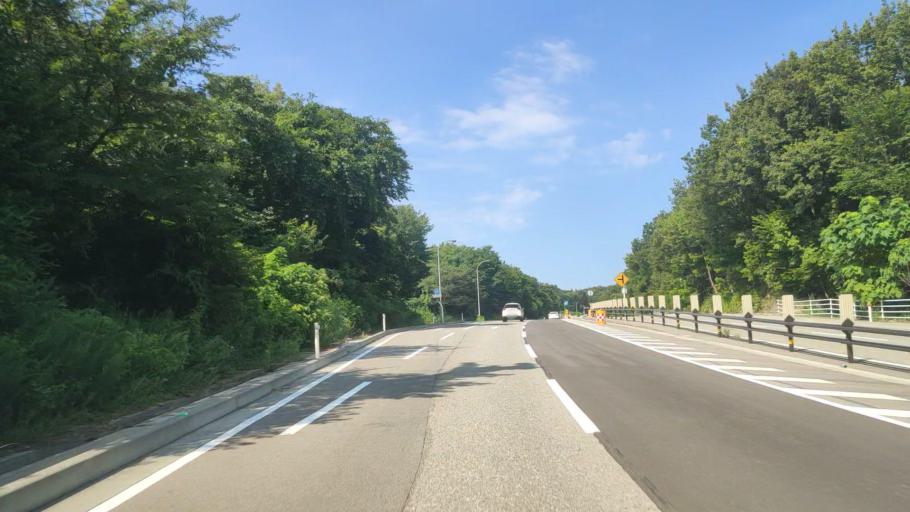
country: JP
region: Ishikawa
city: Komatsu
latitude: 36.4194
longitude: 136.5261
